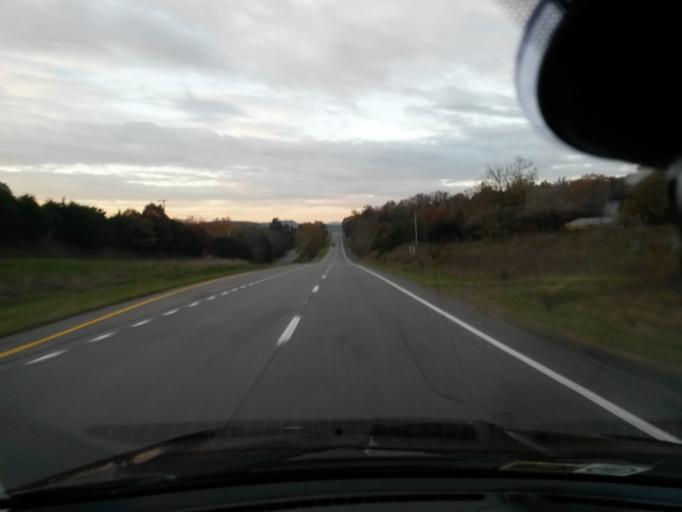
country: US
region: Virginia
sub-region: Botetourt County
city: Fincastle
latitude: 37.5361
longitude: -79.8670
